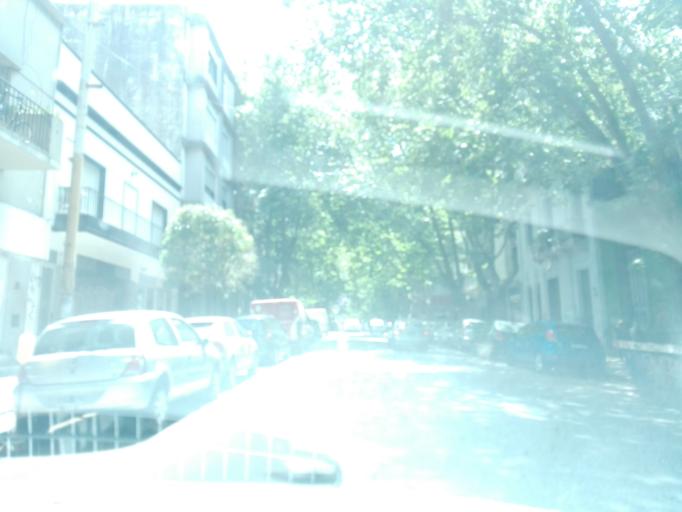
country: AR
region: Buenos Aires
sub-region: Partido de La Plata
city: La Plata
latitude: -34.9174
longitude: -57.9439
